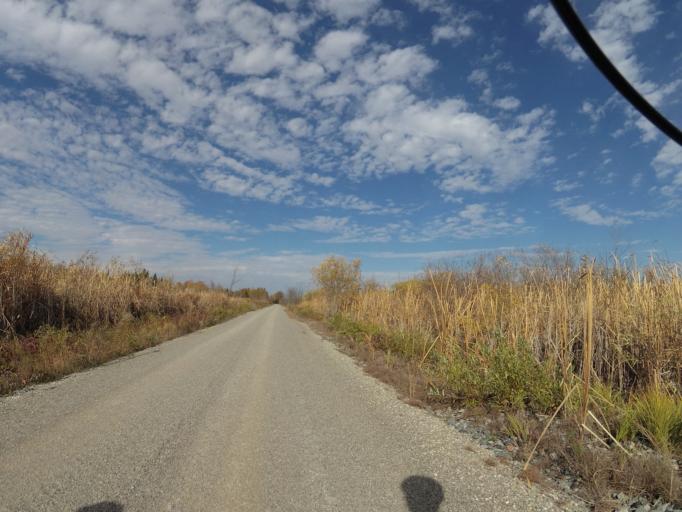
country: CA
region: Ontario
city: Carleton Place
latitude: 45.0268
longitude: -76.0781
